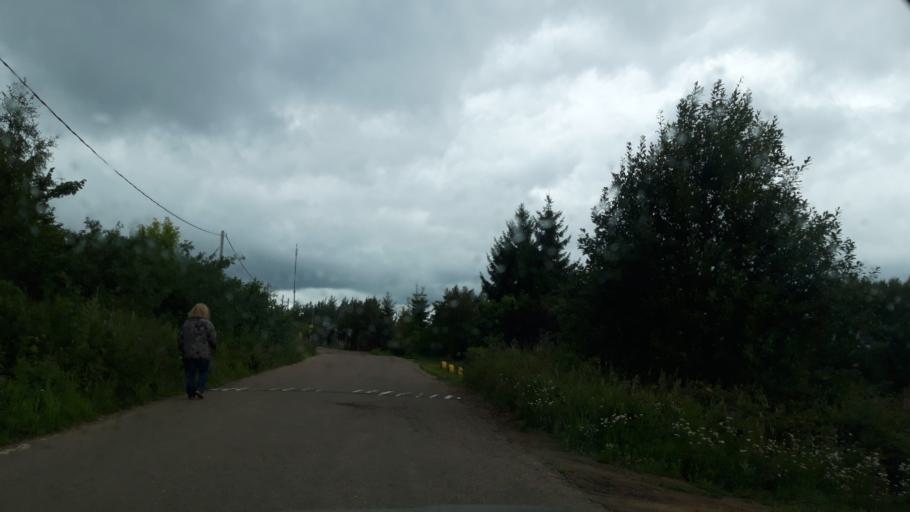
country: RU
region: Moskovskaya
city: Lozhki
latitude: 56.0931
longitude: 37.0744
